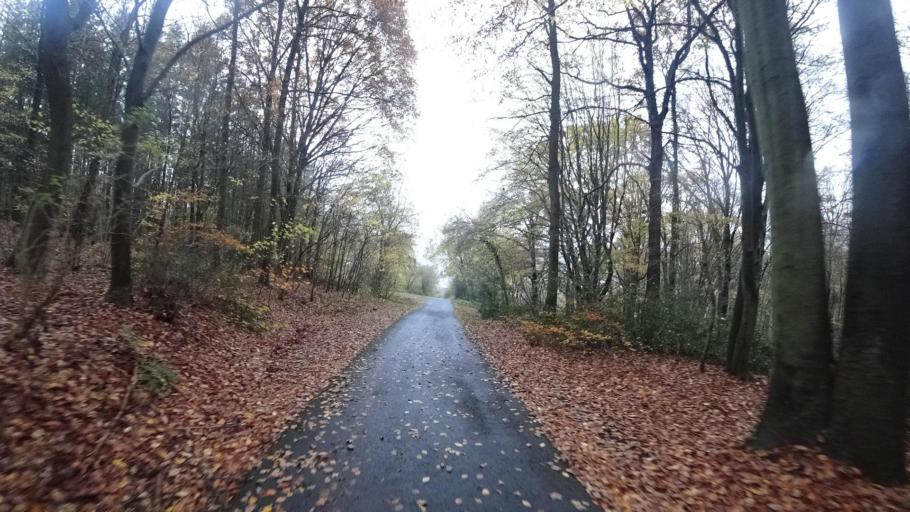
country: DE
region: Rheinland-Pfalz
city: Bad Neuenahr-Ahrweiler
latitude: 50.5362
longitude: 7.1207
